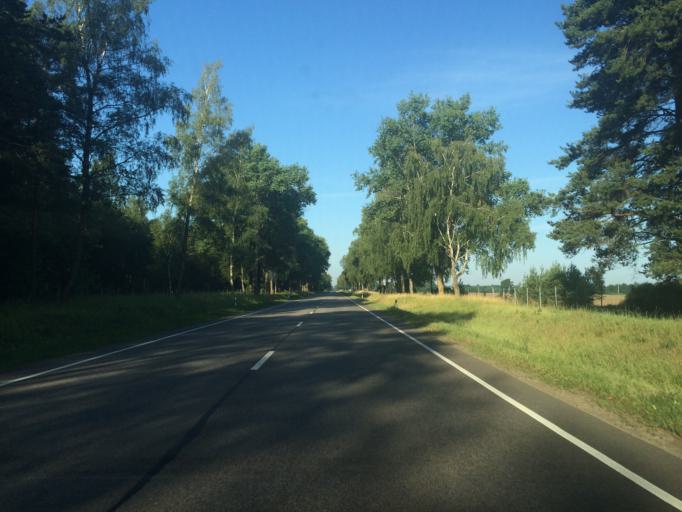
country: LT
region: Kauno apskritis
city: Jonava
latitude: 55.1177
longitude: 24.3747
